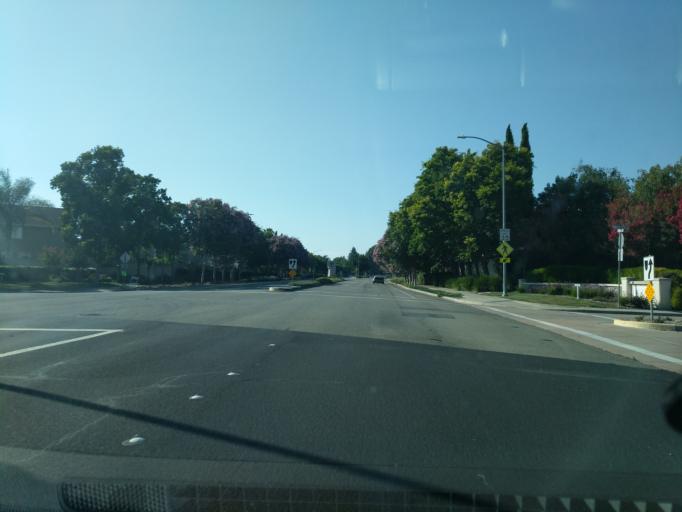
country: US
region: California
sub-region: Alameda County
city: Dublin
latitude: 37.7259
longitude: -121.9292
